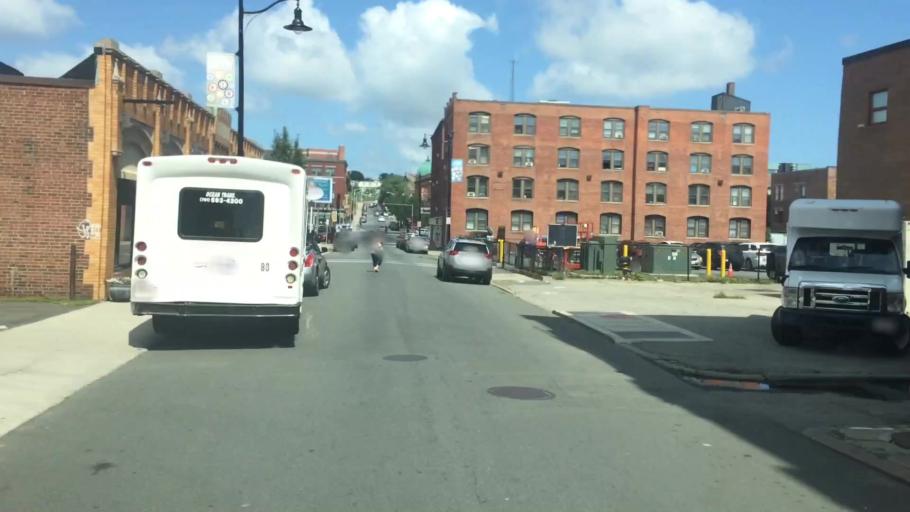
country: US
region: Massachusetts
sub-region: Essex County
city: Lynn
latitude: 42.4634
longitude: -70.9495
